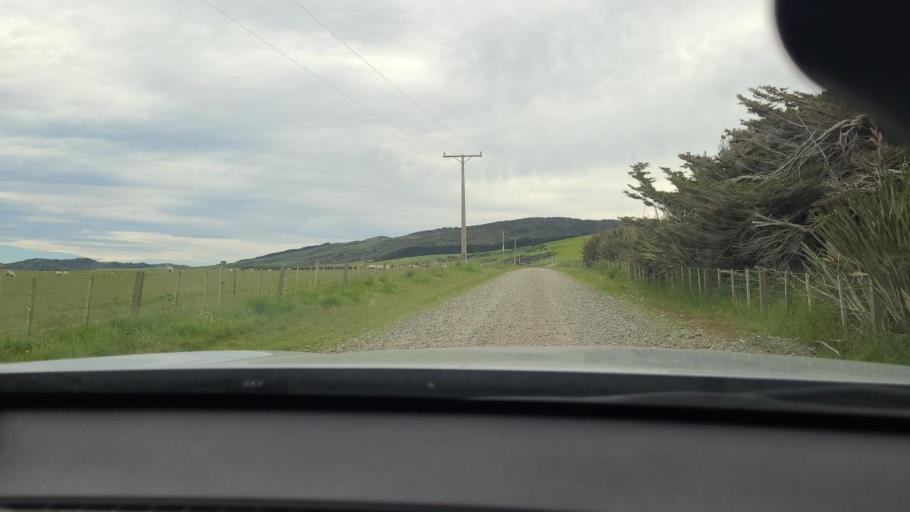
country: NZ
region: Southland
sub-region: Southland District
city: Riverton
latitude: -46.2553
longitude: 167.7152
